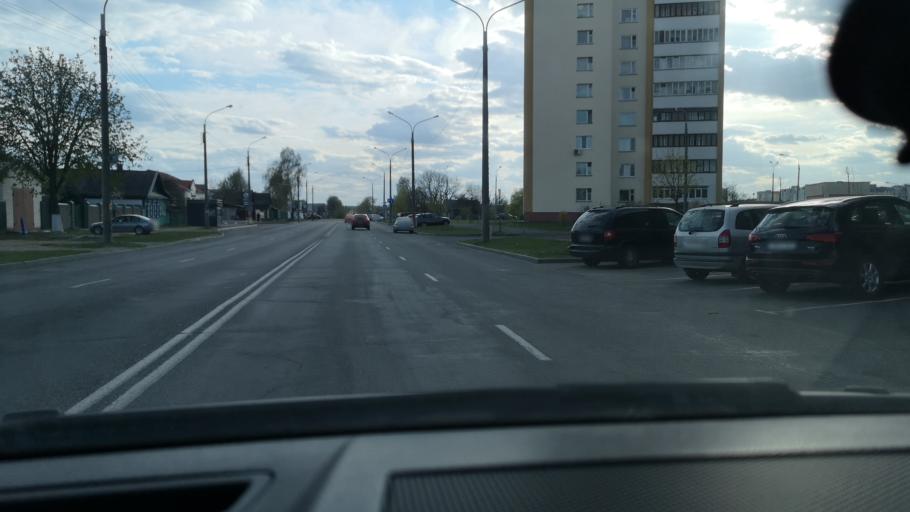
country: BY
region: Gomel
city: Gomel
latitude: 52.4002
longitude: 30.9249
